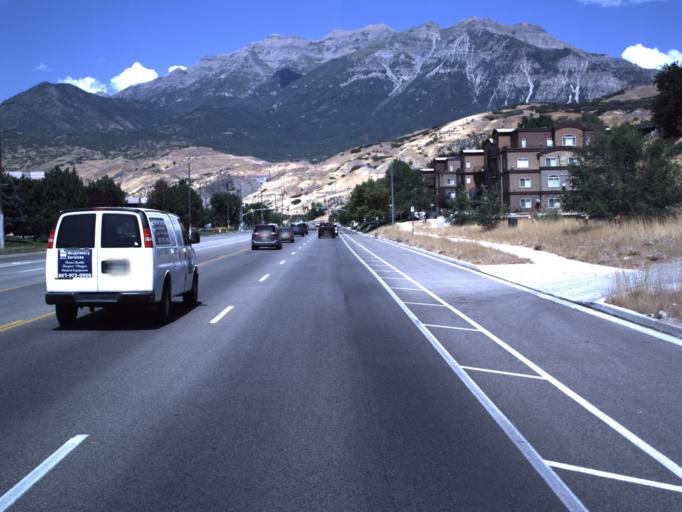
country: US
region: Utah
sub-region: Utah County
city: Orem
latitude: 40.3002
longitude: -111.6563
